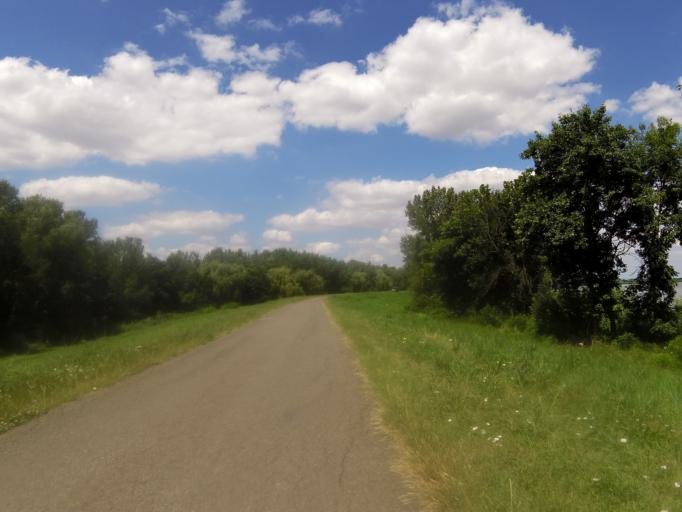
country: HU
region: Heves
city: Tiszanana
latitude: 47.5632
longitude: 20.6118
